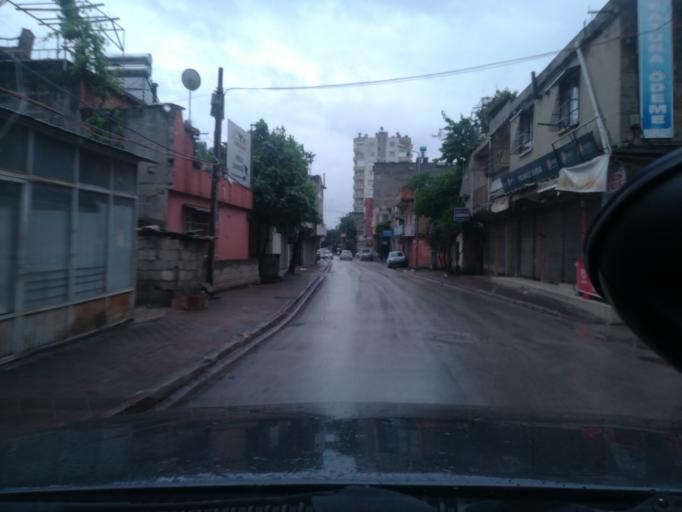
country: TR
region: Adana
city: Seyhan
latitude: 37.0210
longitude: 35.3003
